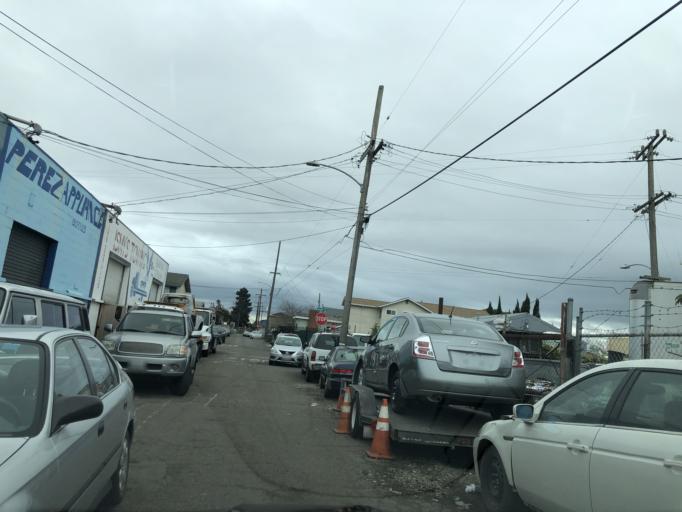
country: US
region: California
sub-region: Alameda County
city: San Leandro
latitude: 37.7491
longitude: -122.1828
